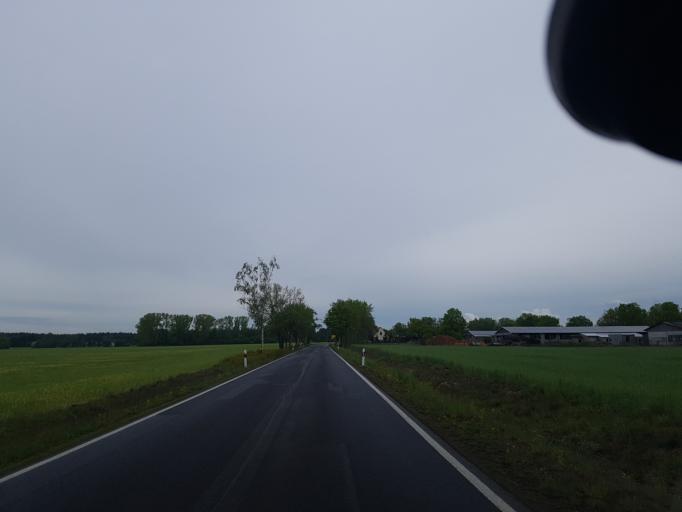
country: DE
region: Brandenburg
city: Spremberg
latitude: 51.6666
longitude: 14.4408
